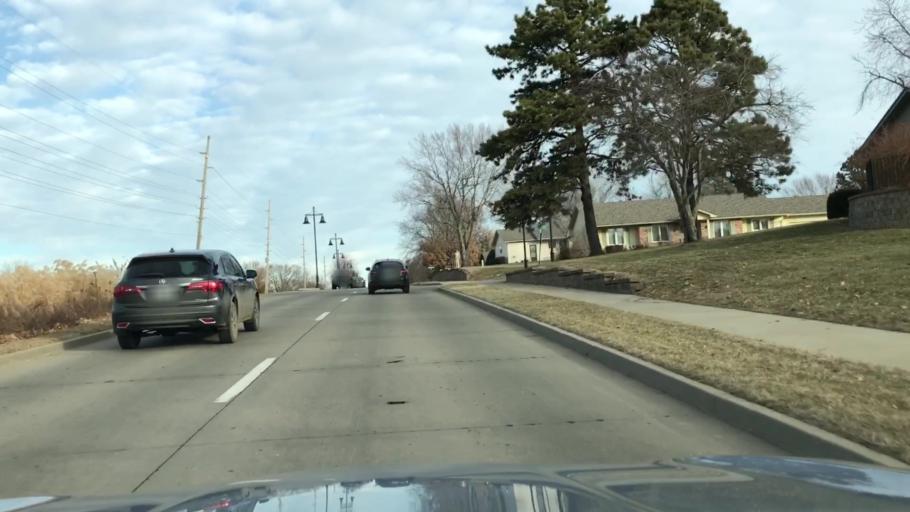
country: US
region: Missouri
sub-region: Jackson County
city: Lees Summit
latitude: 38.9164
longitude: -94.4132
